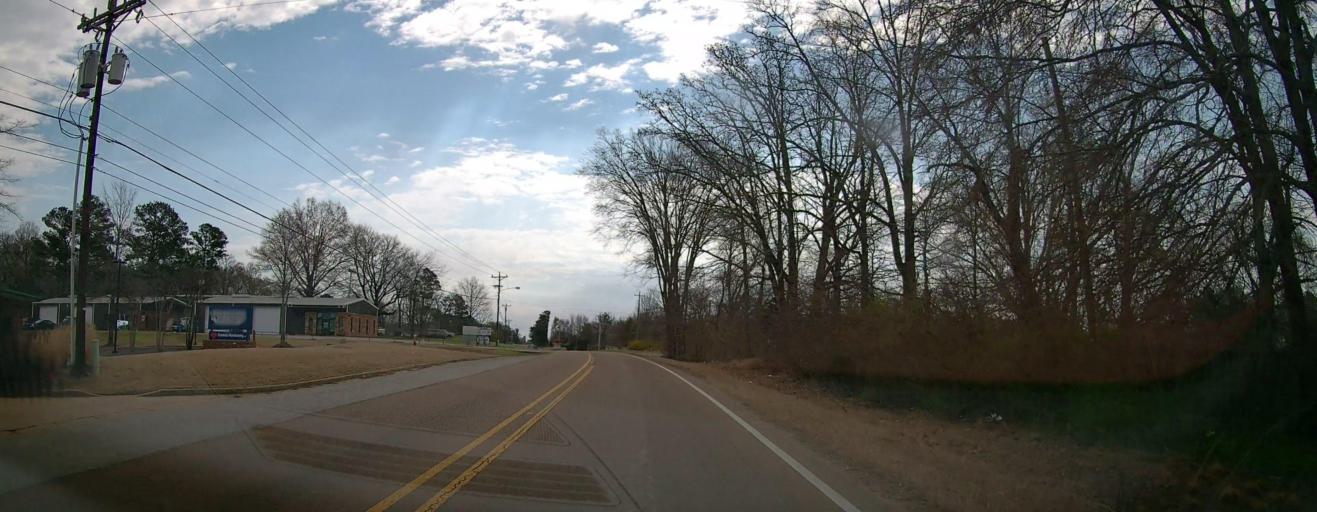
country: US
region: Mississippi
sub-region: De Soto County
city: Olive Branch
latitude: 34.9395
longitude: -89.8041
